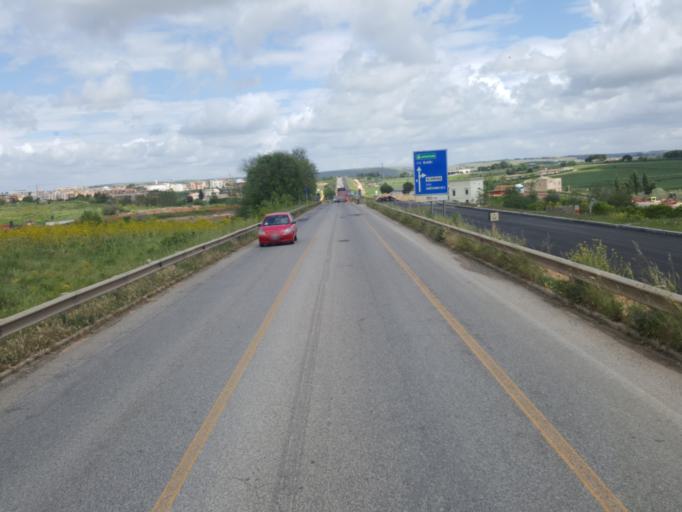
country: IT
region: Apulia
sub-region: Provincia di Bari
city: Altamura
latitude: 40.8225
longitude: 16.5703
